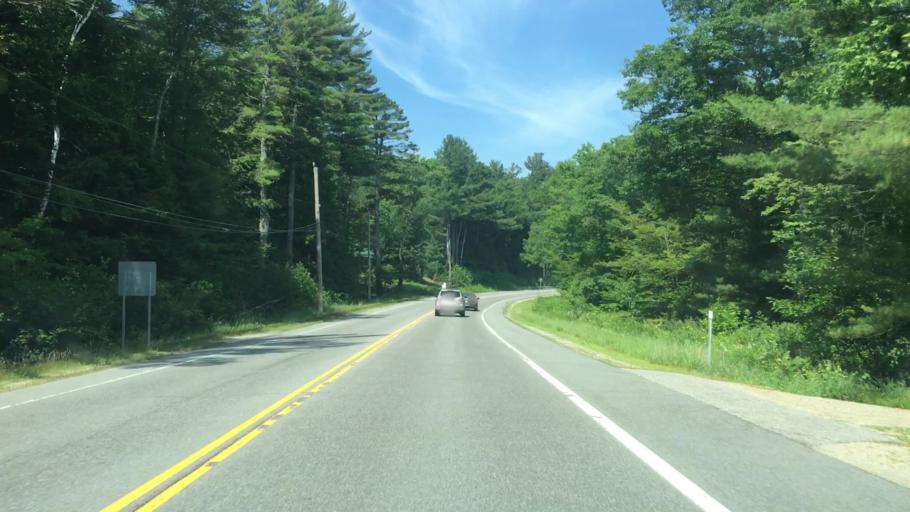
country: US
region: New Hampshire
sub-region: Merrimack County
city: Newbury
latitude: 43.3414
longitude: -72.0783
